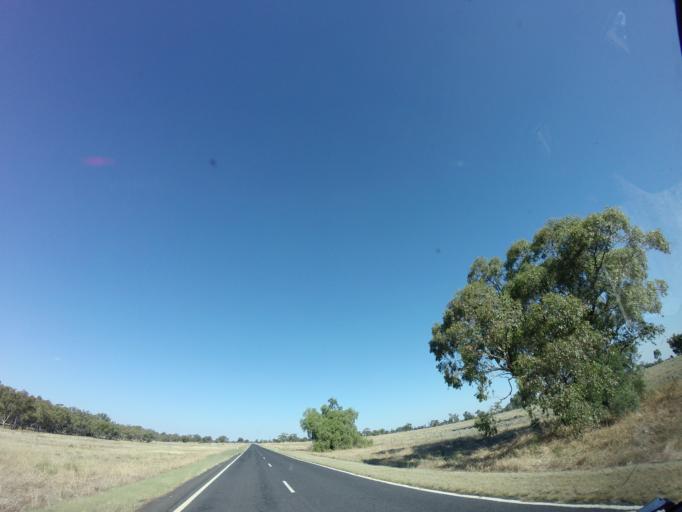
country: AU
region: New South Wales
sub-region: Gilgandra
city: Gilgandra
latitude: -31.6617
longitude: 148.3508
